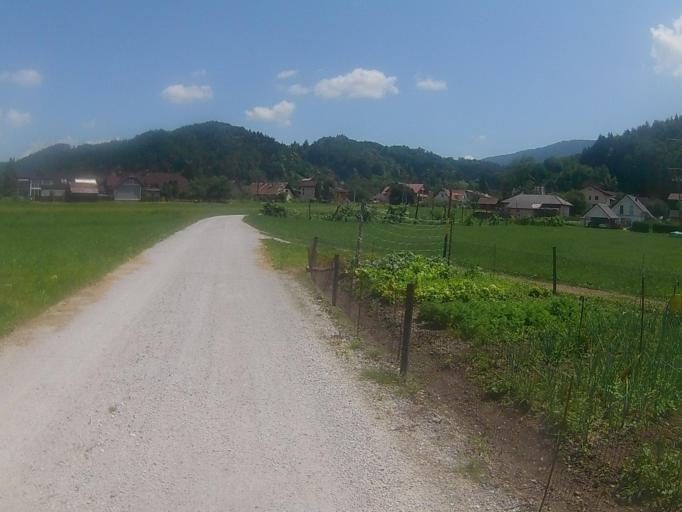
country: SI
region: Ruse
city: Bistrica ob Dravi
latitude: 46.5556
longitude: 15.5452
